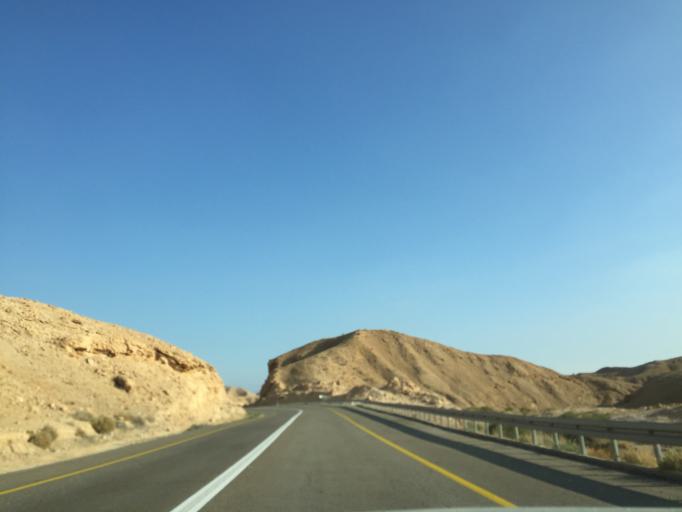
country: IL
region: Southern District
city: `En Boqeq
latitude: 31.1911
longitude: 35.2814
